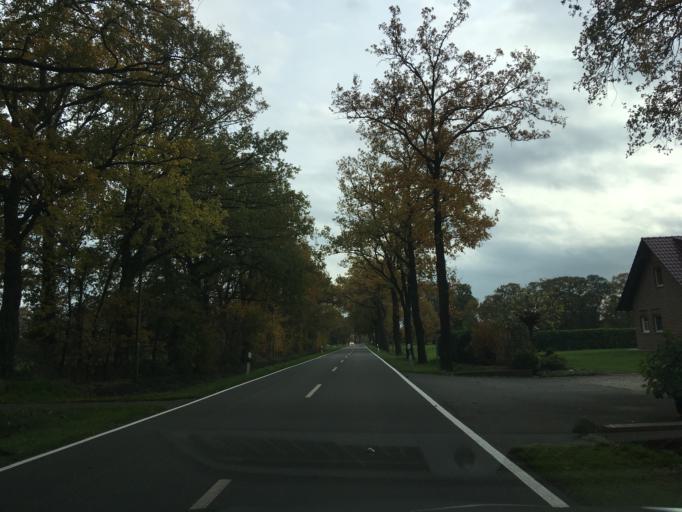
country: DE
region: North Rhine-Westphalia
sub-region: Regierungsbezirk Munster
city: Vreden
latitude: 52.0890
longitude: 6.8911
